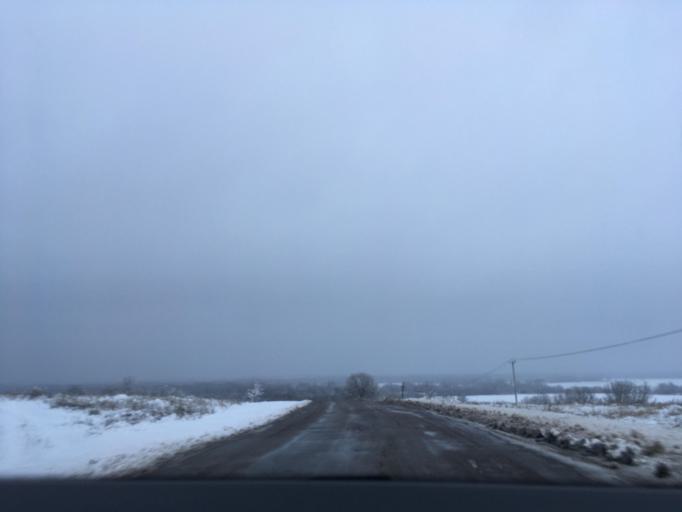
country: RU
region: Voronezj
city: Mitrofanovka
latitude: 50.1358
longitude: 39.9816
